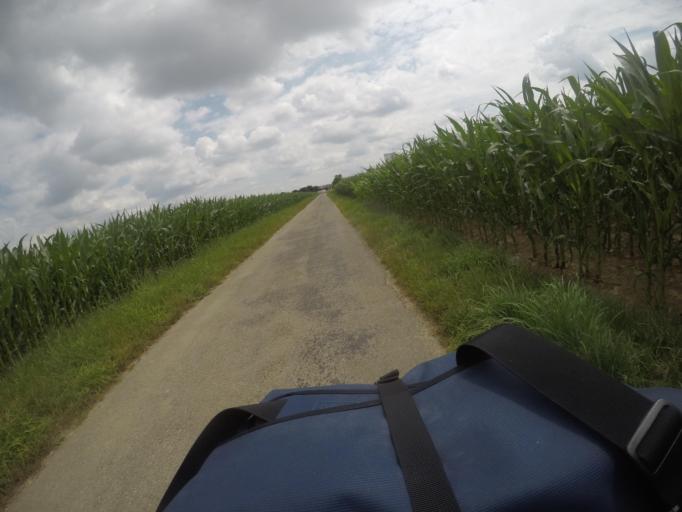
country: DE
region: Bavaria
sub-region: Swabia
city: Memmingen
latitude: 48.0067
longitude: 10.1668
